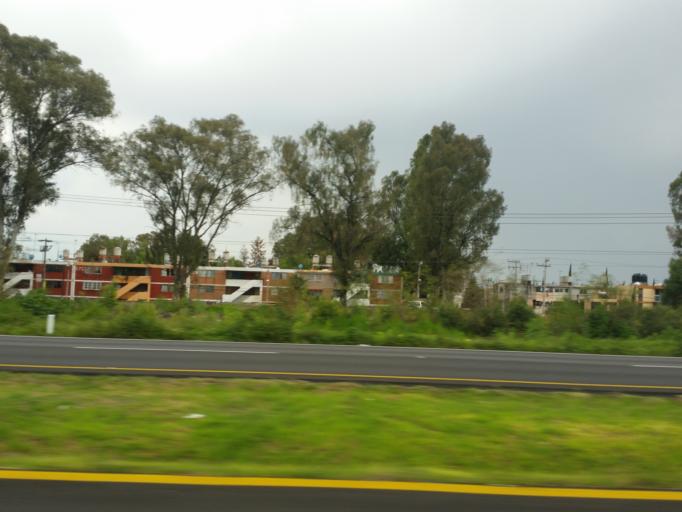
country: MX
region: Mexico
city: Santo Tomas Chiconautla
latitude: 19.6143
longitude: -99.0174
